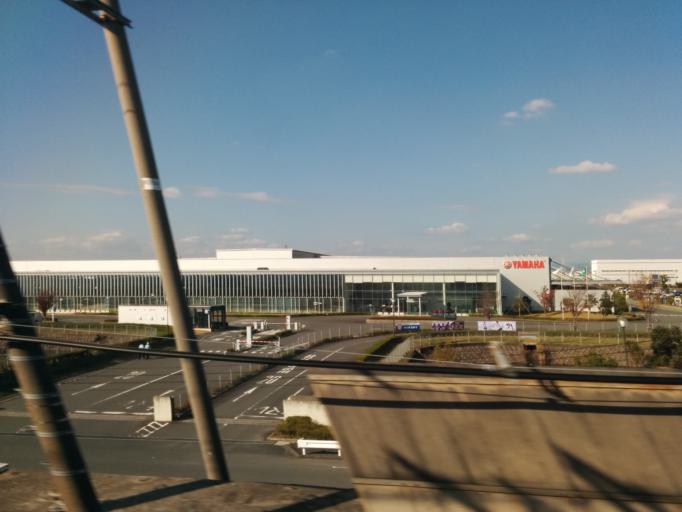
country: JP
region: Shizuoka
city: Fukuroi
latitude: 34.7328
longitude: 137.9132
